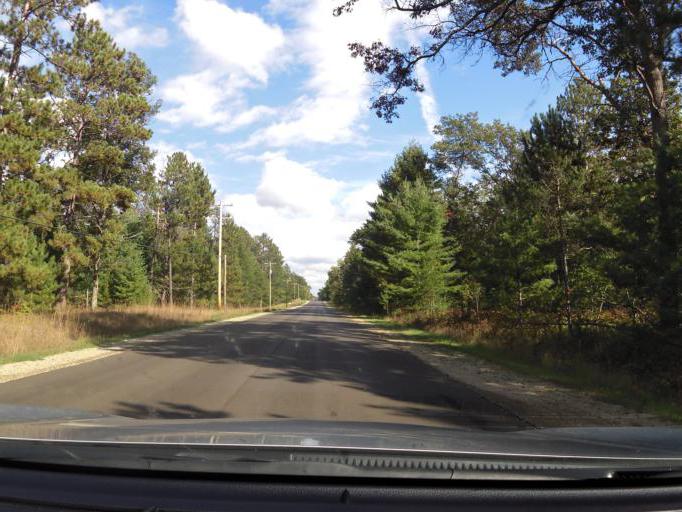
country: US
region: Michigan
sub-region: Roscommon County
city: Roscommon
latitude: 44.5256
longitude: -84.5758
